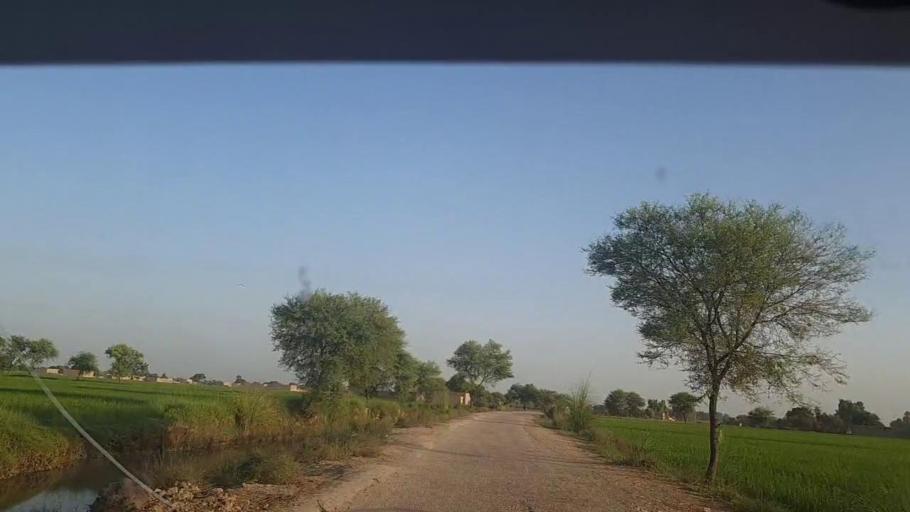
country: PK
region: Sindh
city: Thul
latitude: 28.1220
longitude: 68.8949
